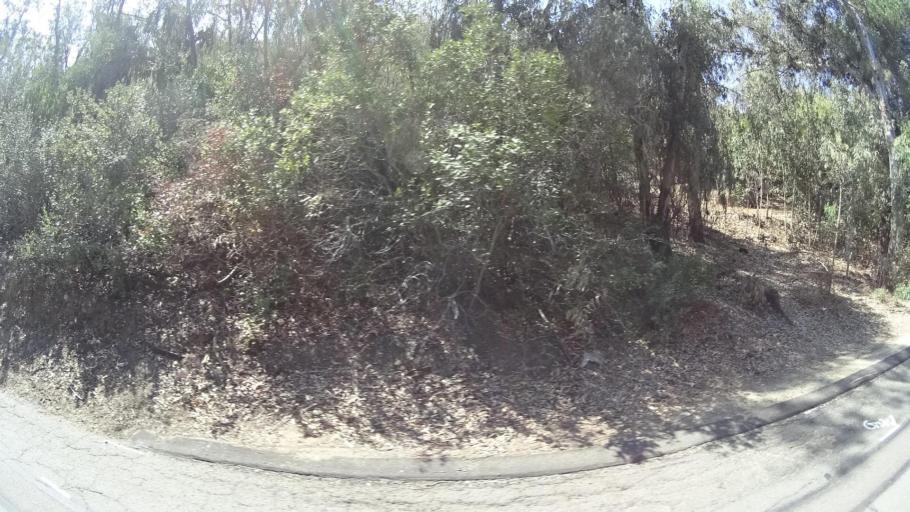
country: US
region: California
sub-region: San Diego County
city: Rancho Santa Fe
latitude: 33.0016
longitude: -117.2178
